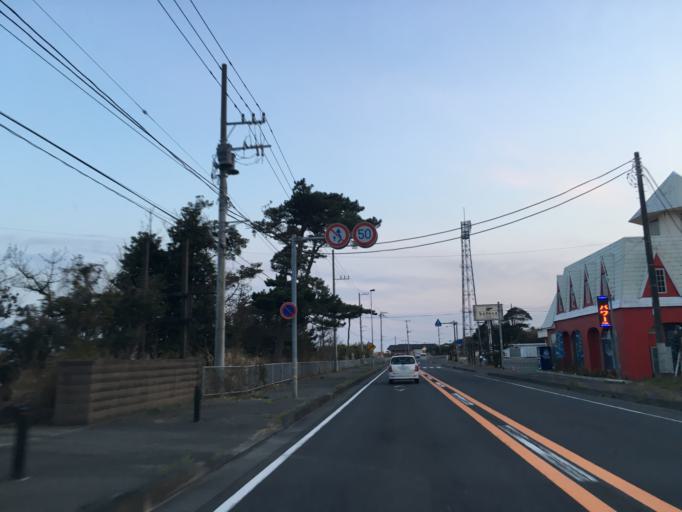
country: JP
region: Ibaraki
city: Kitaibaraki
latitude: 36.7604
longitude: 140.7368
